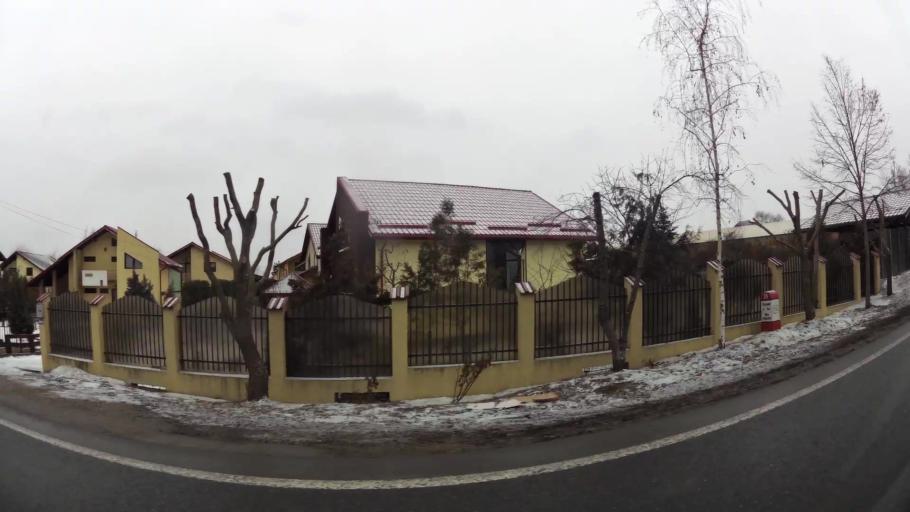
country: RO
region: Dambovita
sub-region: Comuna Aninoasa
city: Viforata
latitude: 44.9502
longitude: 25.4808
